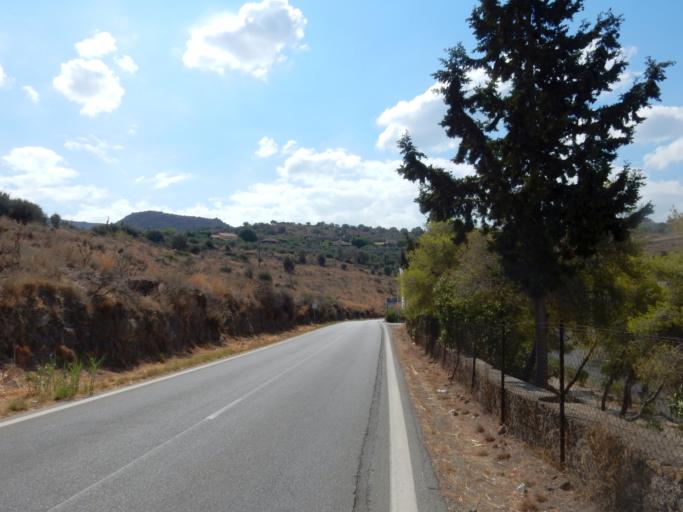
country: GR
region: Attica
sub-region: Nomos Piraios
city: Aegina
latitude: 37.6954
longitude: 23.4651
